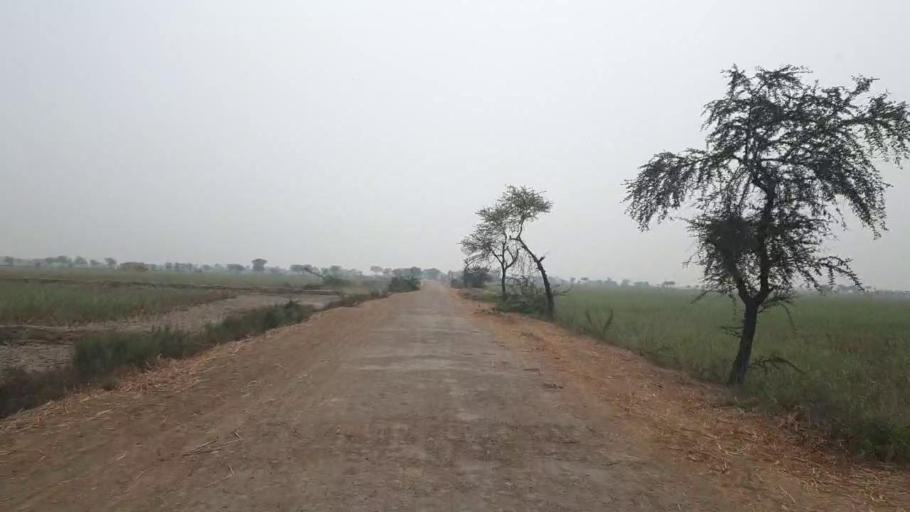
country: PK
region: Sindh
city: Kario
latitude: 24.6500
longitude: 68.6217
